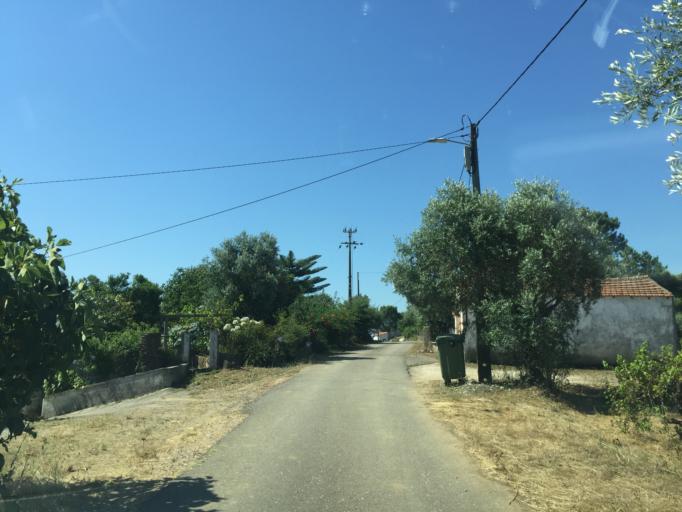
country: PT
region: Santarem
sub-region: Ferreira do Zezere
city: Ferreira do Zezere
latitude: 39.5854
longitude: -8.2765
